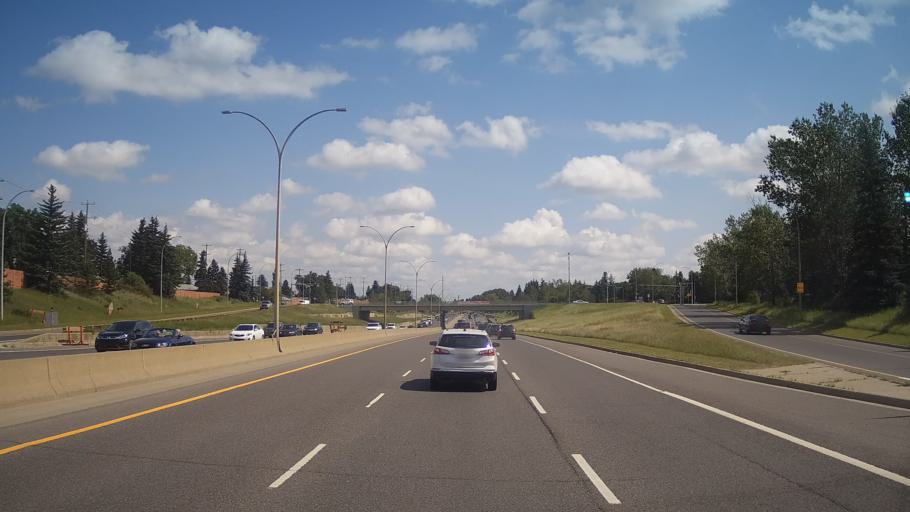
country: CA
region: Alberta
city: St. Albert
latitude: 53.5120
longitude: -113.6004
